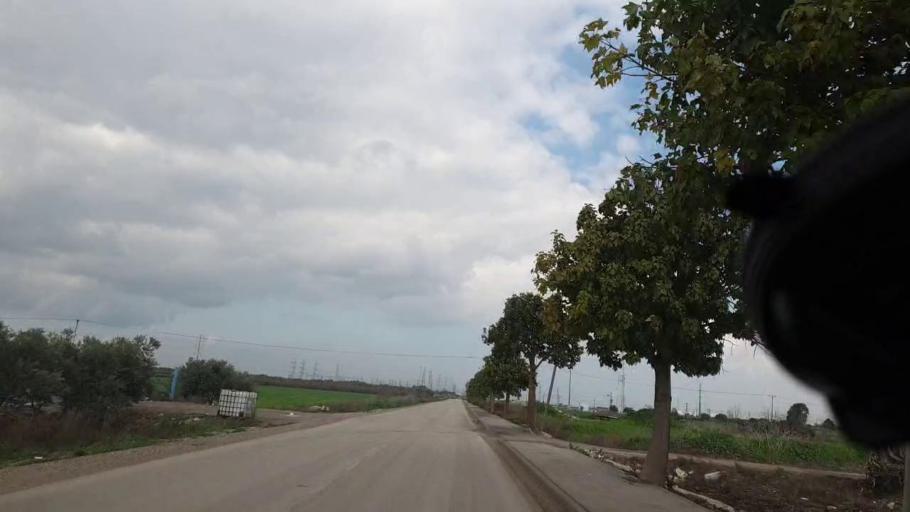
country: IL
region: Haifa
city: Rekhasim
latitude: 32.7510
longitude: 35.0876
